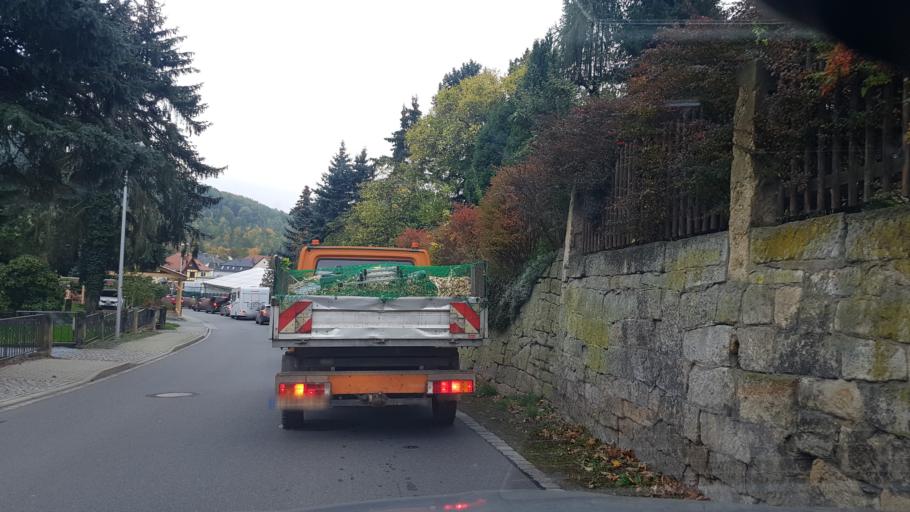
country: DE
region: Saxony
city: Dohma
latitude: 50.9205
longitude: 13.9752
